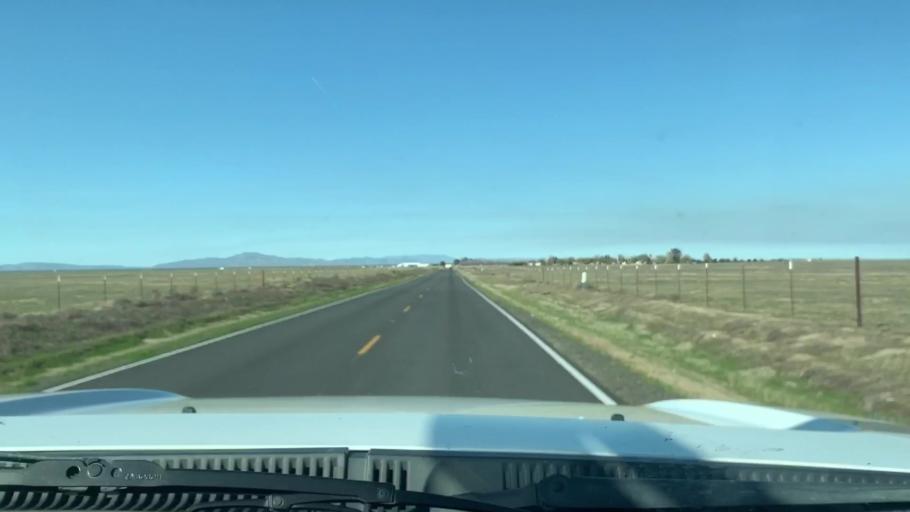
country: US
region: California
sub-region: Kern County
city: Lost Hills
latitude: 35.6025
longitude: -119.8525
